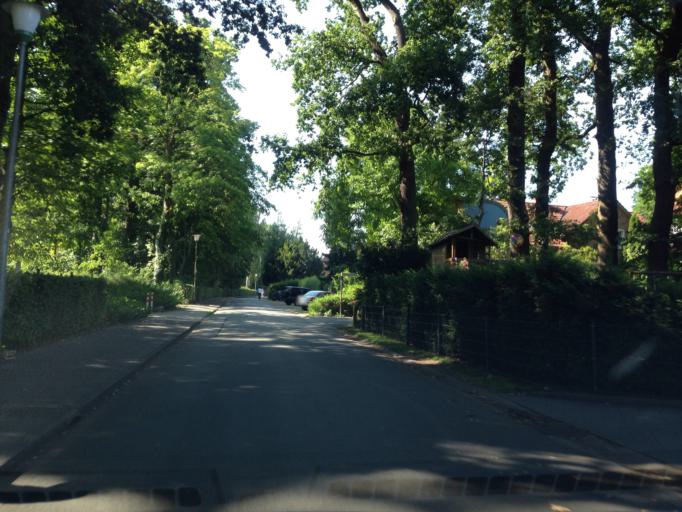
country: DE
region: North Rhine-Westphalia
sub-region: Regierungsbezirk Munster
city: Muenster
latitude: 51.9793
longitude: 7.6197
